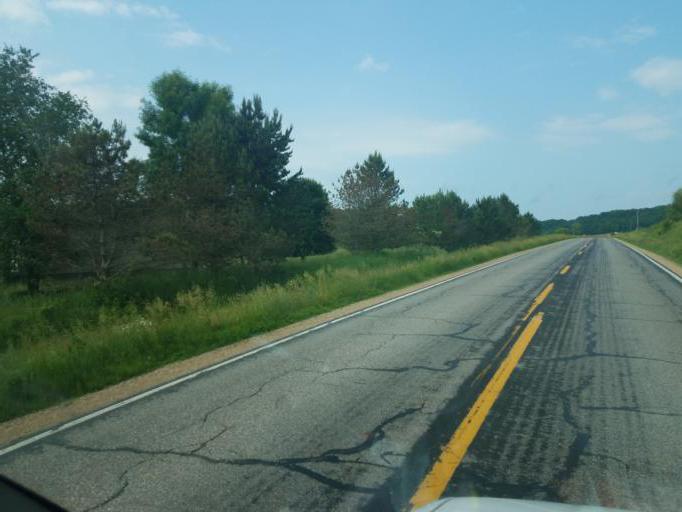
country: US
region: Wisconsin
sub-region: Vernon County
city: Hillsboro
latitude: 43.6468
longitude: -90.4058
